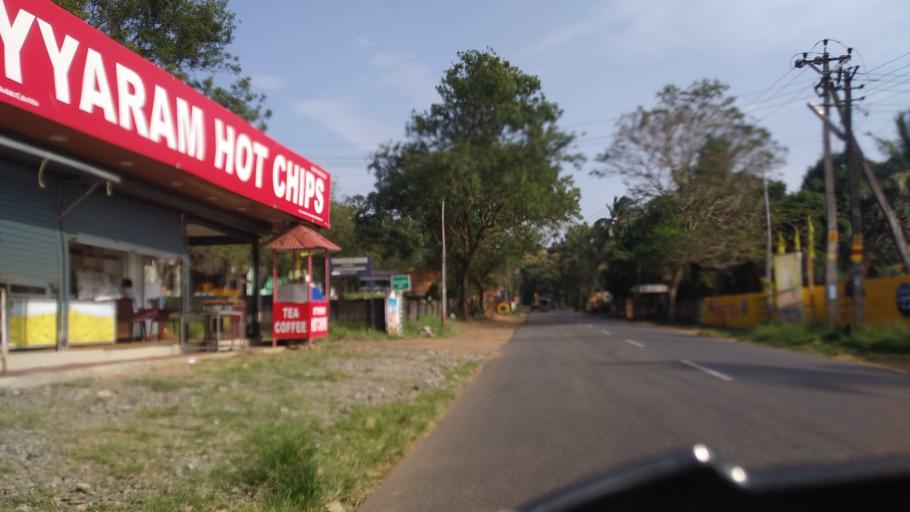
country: IN
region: Kerala
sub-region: Thrissur District
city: Chelakara
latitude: 10.5988
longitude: 76.4971
